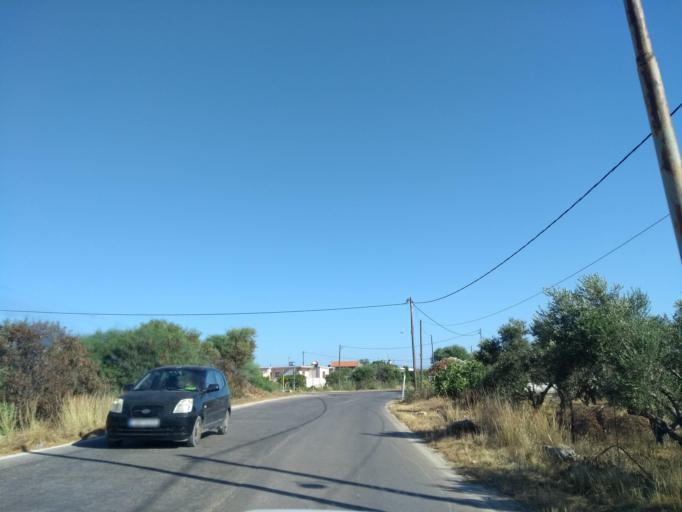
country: GR
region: Crete
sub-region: Nomos Chanias
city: Pithari
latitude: 35.5803
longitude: 24.0933
